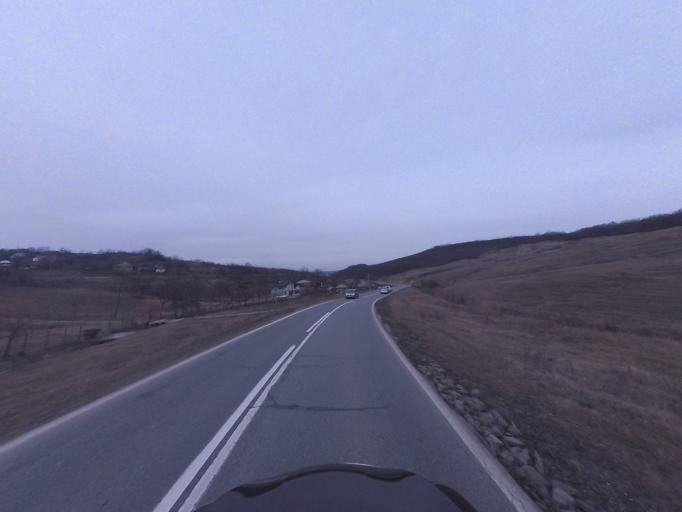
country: RO
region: Iasi
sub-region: Comuna Popricani
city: Popricani
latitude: 47.2949
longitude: 27.5098
